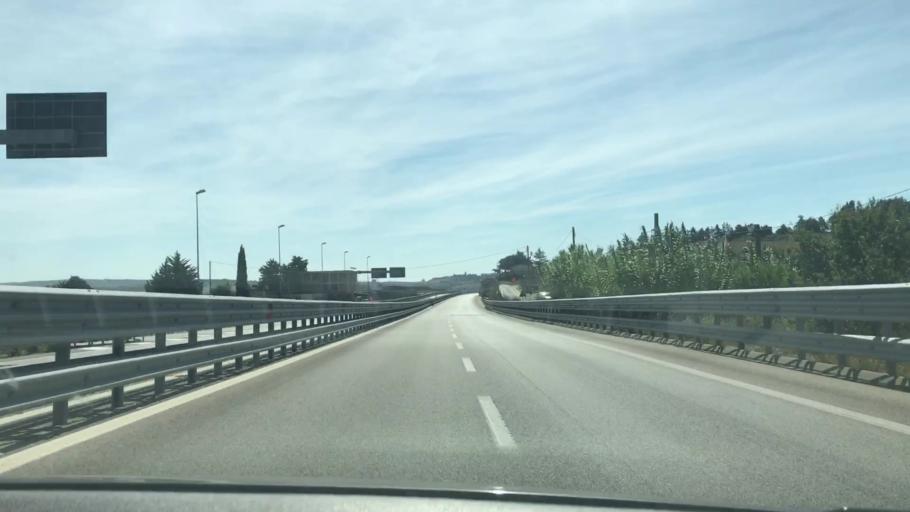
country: IT
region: Basilicate
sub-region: Provincia di Matera
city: Matera
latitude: 40.6987
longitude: 16.5888
